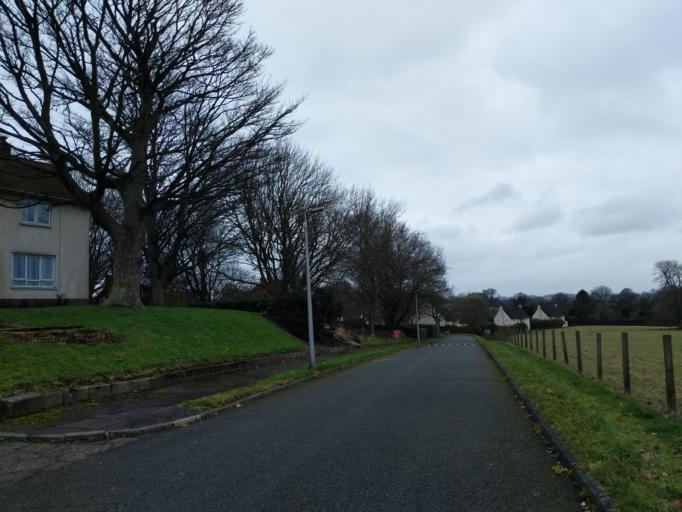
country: GB
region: Scotland
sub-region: Edinburgh
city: Ratho
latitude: 55.9650
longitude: -3.3267
